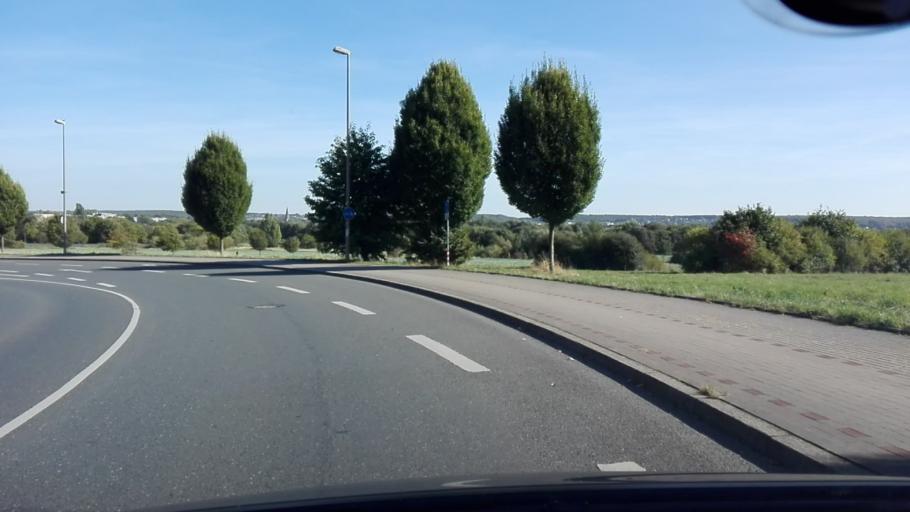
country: DE
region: North Rhine-Westphalia
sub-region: Regierungsbezirk Arnsberg
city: Dortmund
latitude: 51.5061
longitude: 7.5347
